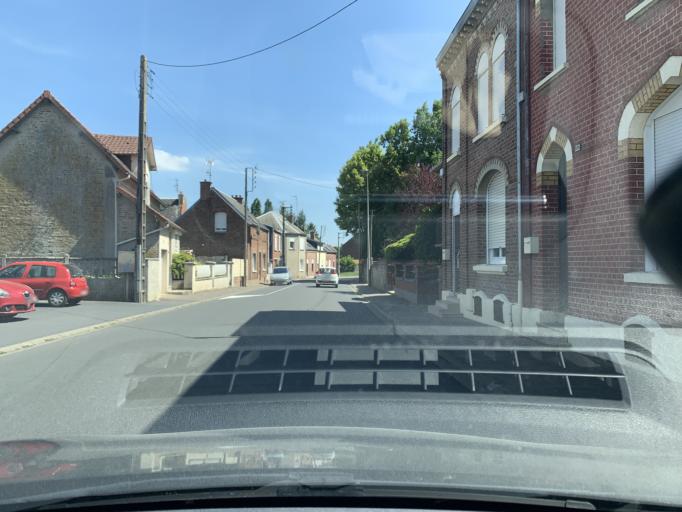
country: FR
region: Nord-Pas-de-Calais
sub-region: Departement du Nord
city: Caudry
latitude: 50.1243
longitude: 3.3994
